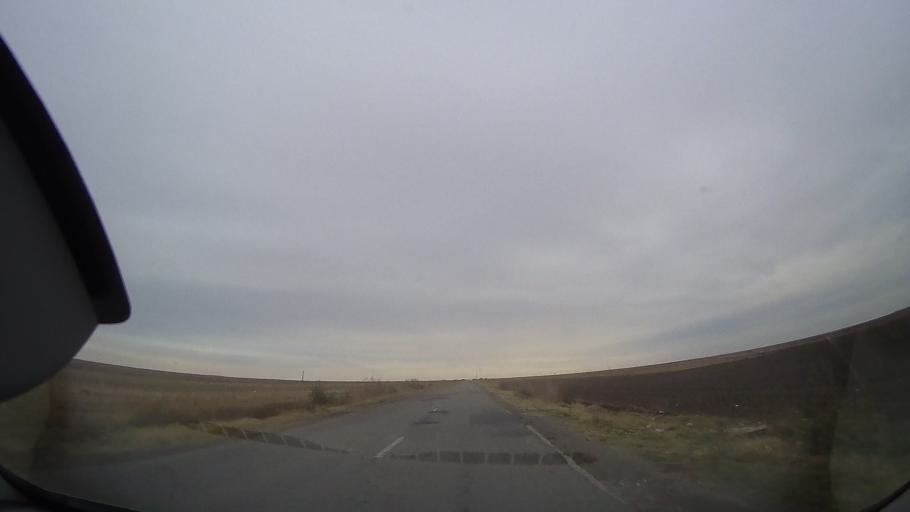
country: RO
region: Ialomita
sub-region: Oras Amara
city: Amara
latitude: 44.6568
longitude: 27.3007
